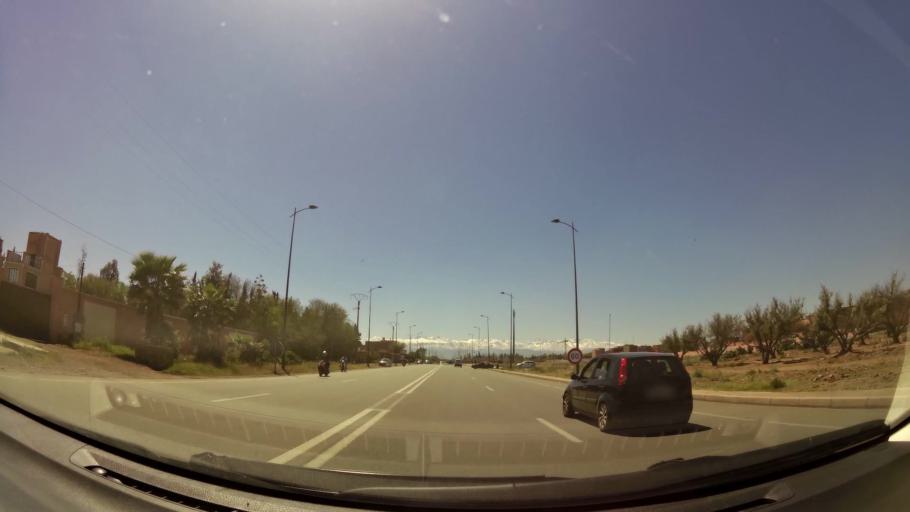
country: MA
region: Marrakech-Tensift-Al Haouz
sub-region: Marrakech
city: Marrakesh
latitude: 31.5558
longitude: -7.9762
